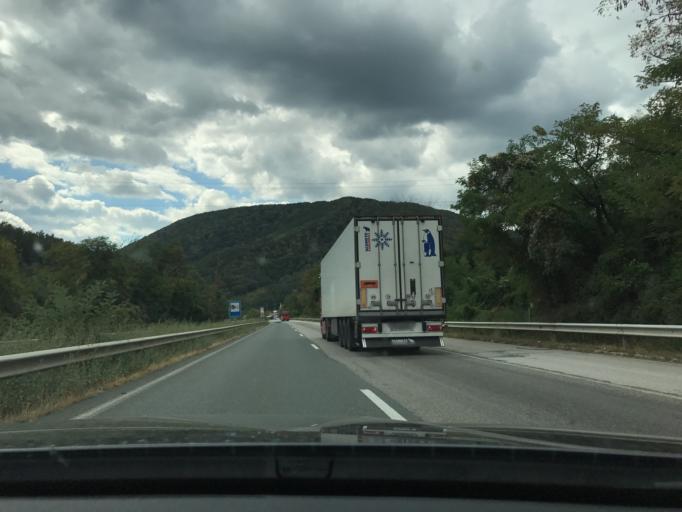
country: BG
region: Sofiya
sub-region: Obshtina Botevgrad
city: Botevgrad
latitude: 42.8814
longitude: 23.8075
